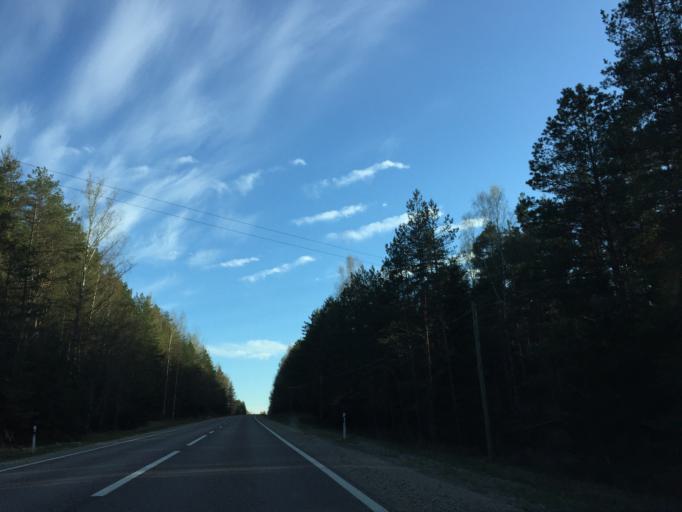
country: LV
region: Valkas Rajons
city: Valka
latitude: 57.7345
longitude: 25.9430
